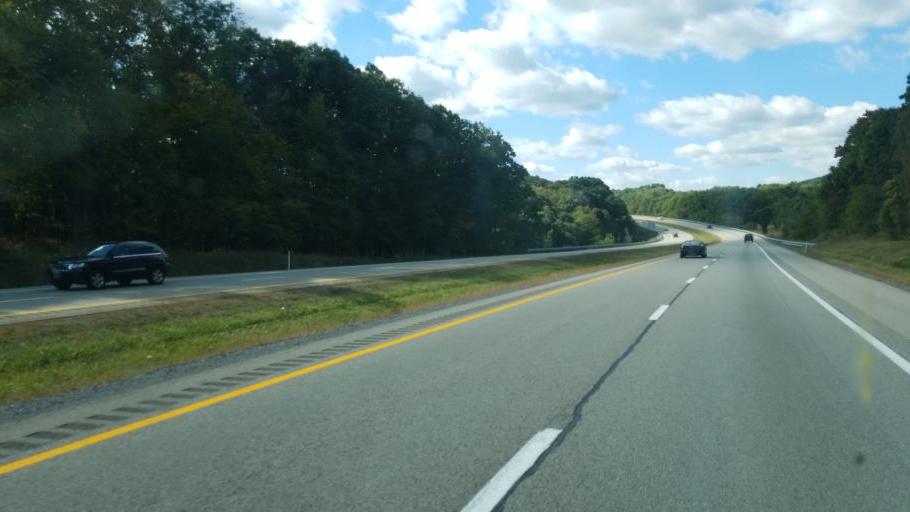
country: US
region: Pennsylvania
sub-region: Fayette County
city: Fairchance
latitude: 39.6601
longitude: -79.6625
